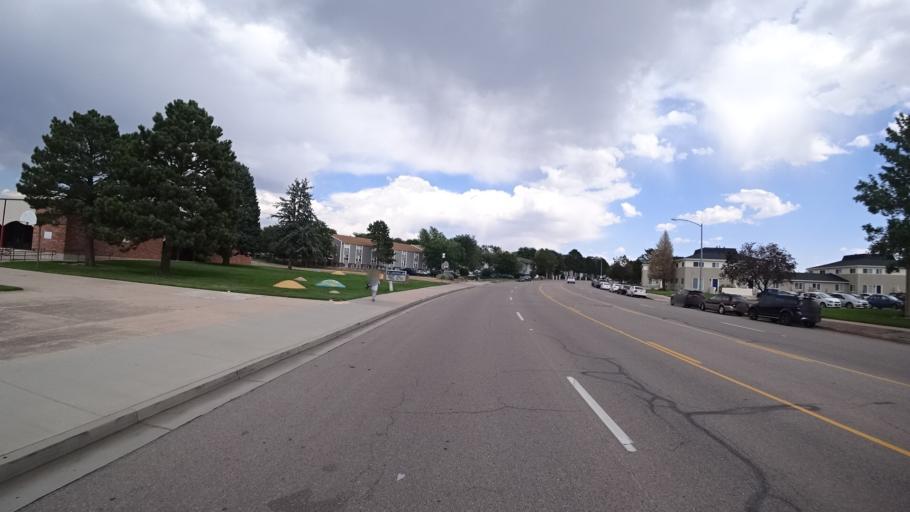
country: US
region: Colorado
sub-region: El Paso County
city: Cimarron Hills
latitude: 38.8346
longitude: -104.7499
